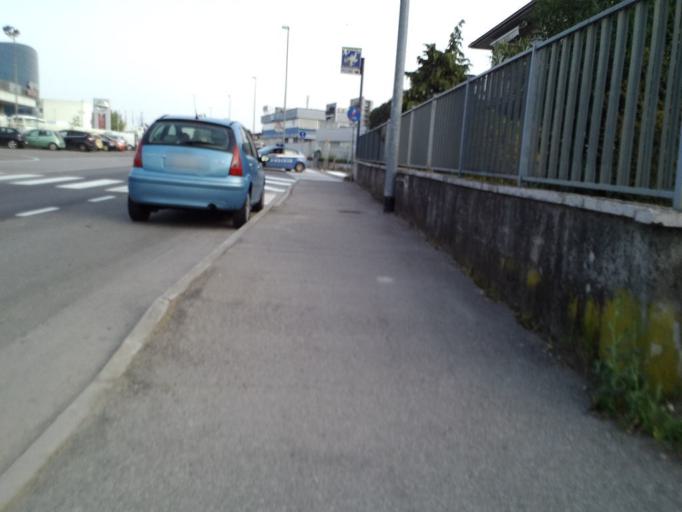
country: IT
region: Veneto
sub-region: Provincia di Verona
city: Verona
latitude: 45.4115
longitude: 10.9553
